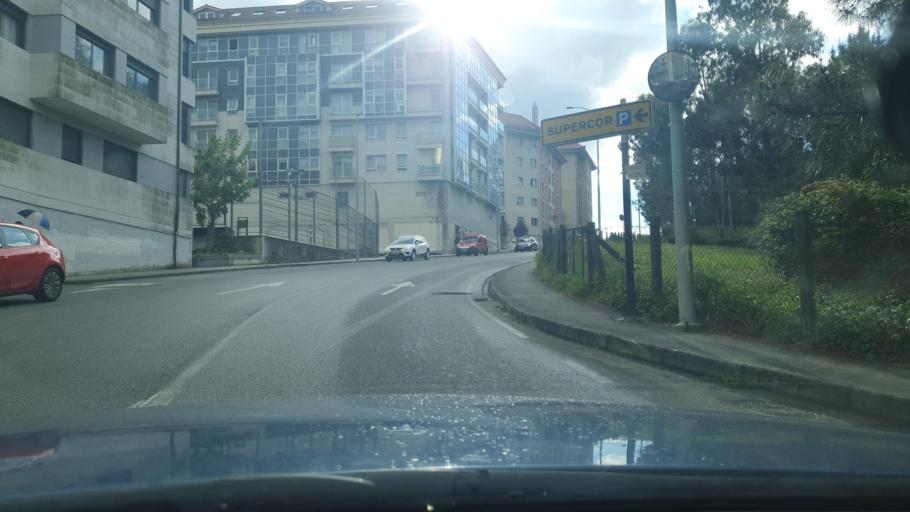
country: ES
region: Galicia
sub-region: Provincia da Coruna
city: Santiago de Compostela
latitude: 42.8482
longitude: -8.5780
